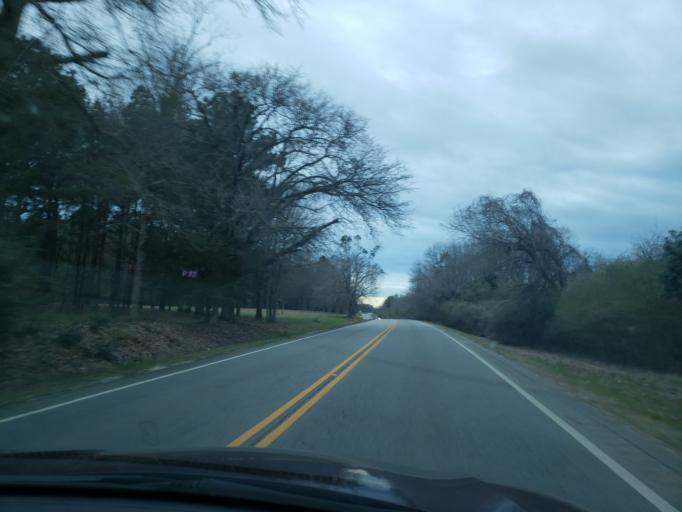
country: US
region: Alabama
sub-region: Chambers County
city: Lafayette
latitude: 32.9376
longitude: -85.3964
